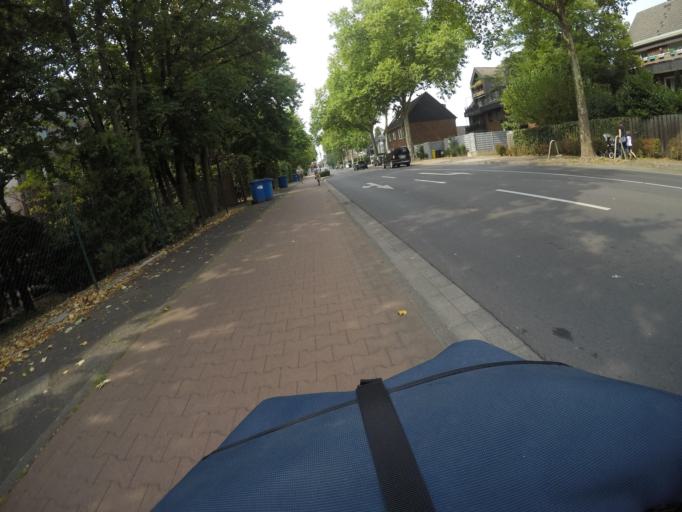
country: DE
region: North Rhine-Westphalia
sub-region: Regierungsbezirk Dusseldorf
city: Meerbusch
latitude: 51.2550
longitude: 6.6850
